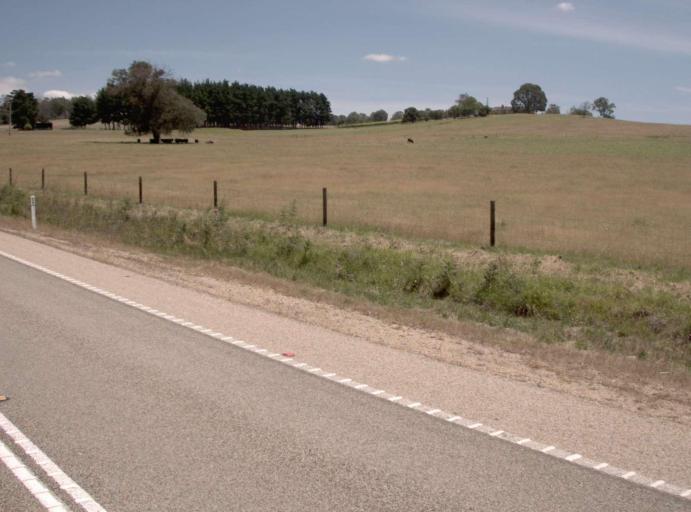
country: AU
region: Victoria
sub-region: East Gippsland
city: Bairnsdale
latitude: -37.7664
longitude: 147.6967
